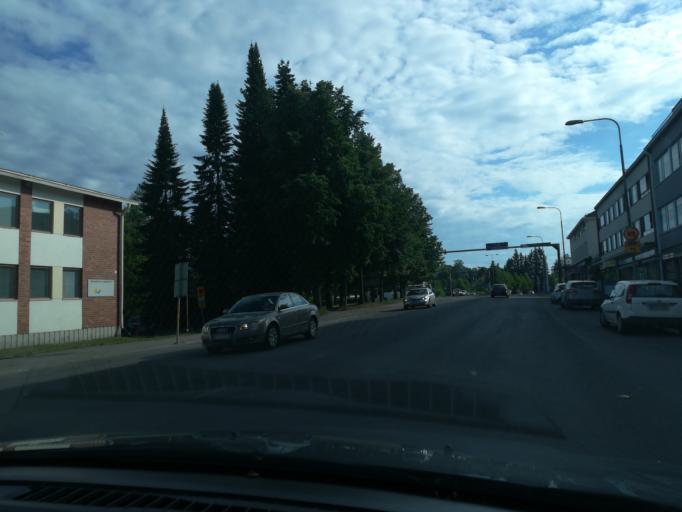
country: FI
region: South Karelia
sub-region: Imatra
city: Imatra
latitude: 61.1714
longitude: 28.7734
